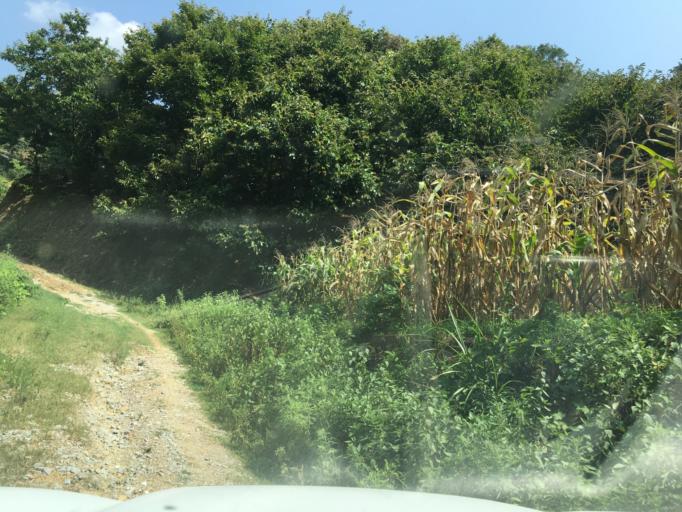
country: CN
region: Guangxi Zhuangzu Zizhiqu
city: Xinzhou
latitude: 24.9919
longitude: 105.7427
